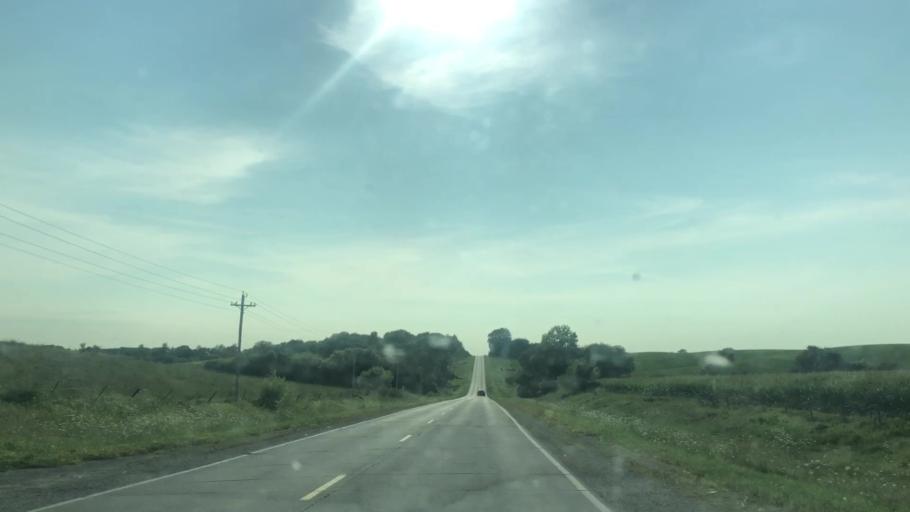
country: US
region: Iowa
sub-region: Marshall County
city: Marshalltown
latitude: 42.0491
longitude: -92.9674
